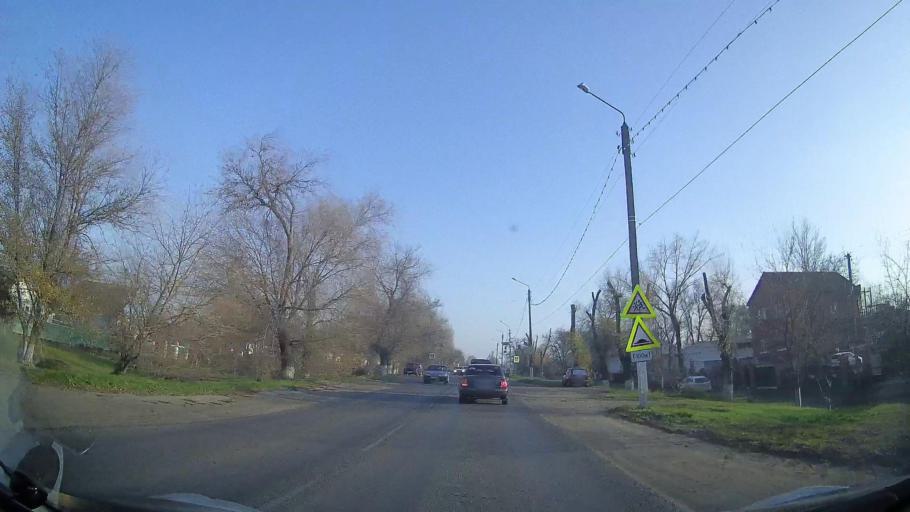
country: RU
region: Rostov
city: Ol'ginskaya
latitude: 47.1883
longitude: 39.9505
